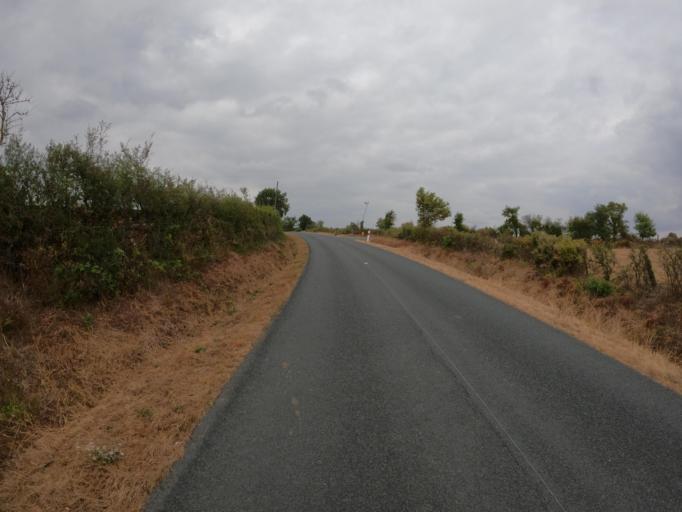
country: FR
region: Pays de la Loire
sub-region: Departement de la Vendee
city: Tiffauges
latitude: 47.0007
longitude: -1.1078
